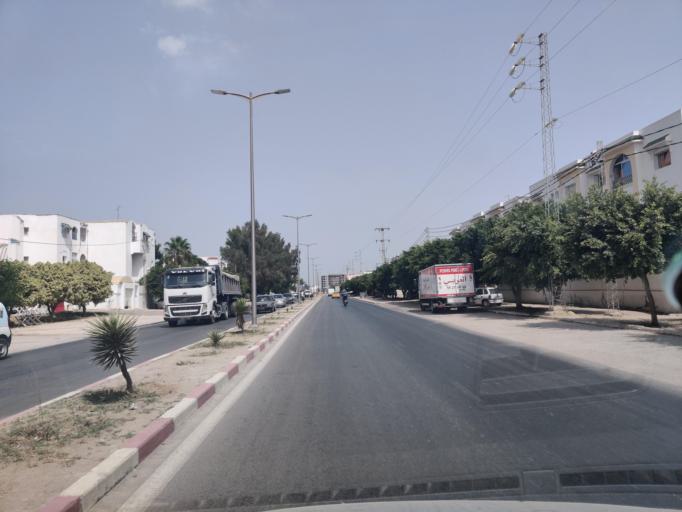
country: TN
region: Nabul
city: Bu `Urqub
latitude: 36.5886
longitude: 10.5056
